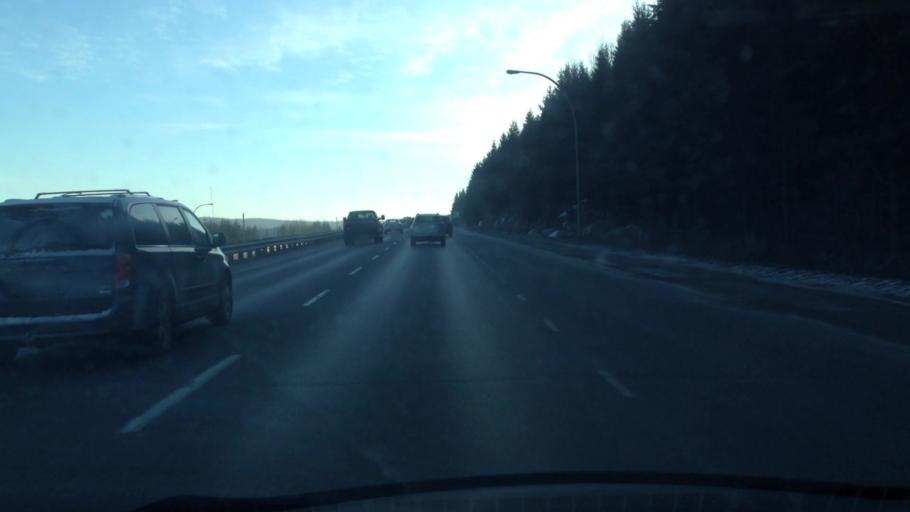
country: CA
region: Quebec
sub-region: Laurentides
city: Prevost
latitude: 45.8821
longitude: -74.1029
